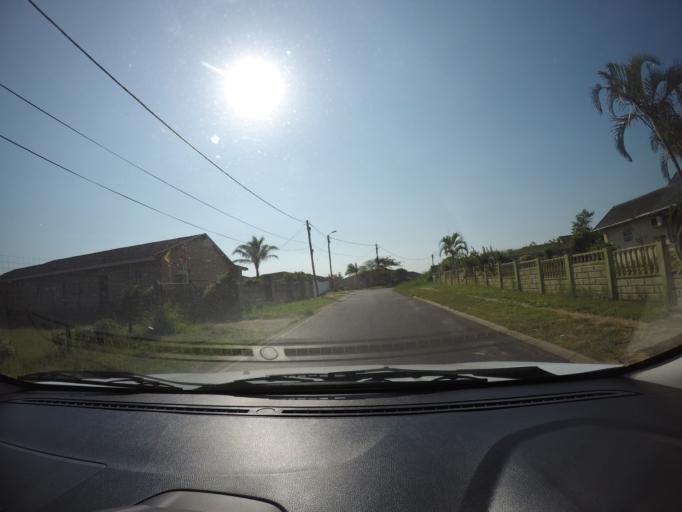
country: ZA
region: KwaZulu-Natal
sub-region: uThungulu District Municipality
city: Richards Bay
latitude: -28.7197
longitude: 32.0416
